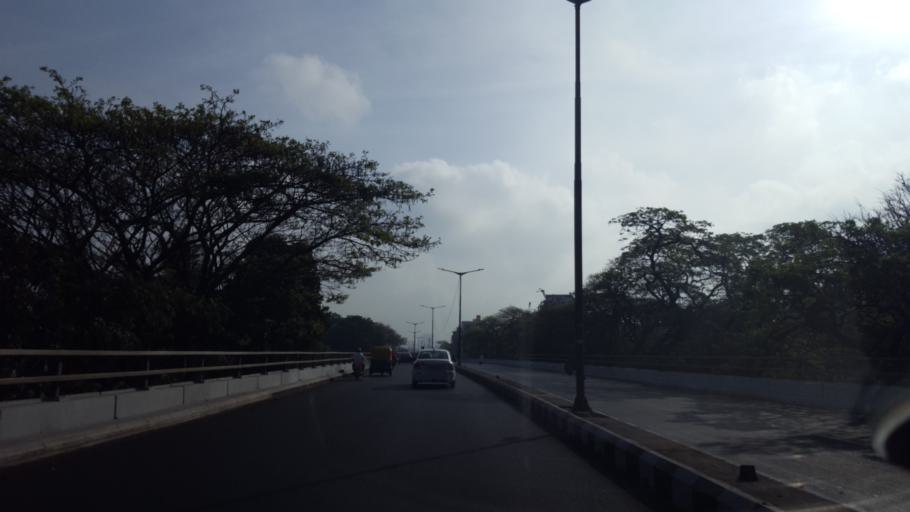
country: IN
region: Karnataka
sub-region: Bangalore Urban
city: Bangalore
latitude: 12.9618
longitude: 77.5628
